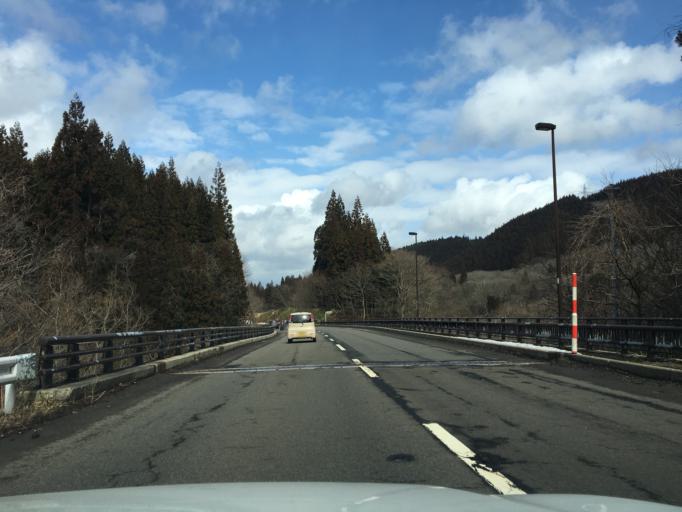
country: JP
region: Akita
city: Takanosu
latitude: 40.0120
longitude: 140.2788
